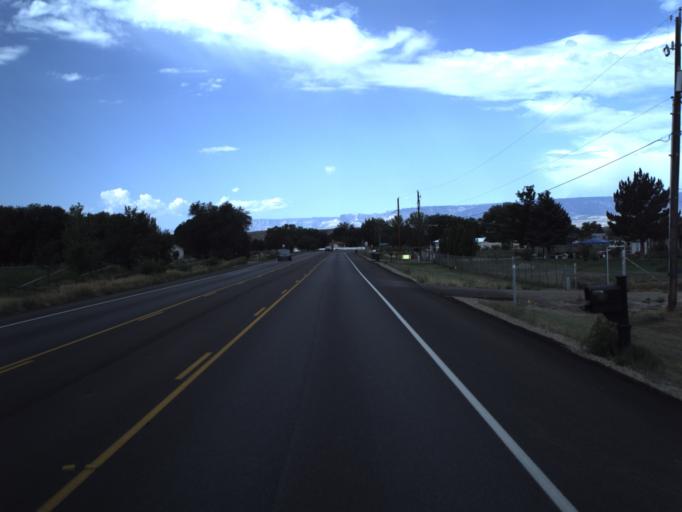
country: US
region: Utah
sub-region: Carbon County
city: Wellington
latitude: 39.5443
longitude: -110.6804
